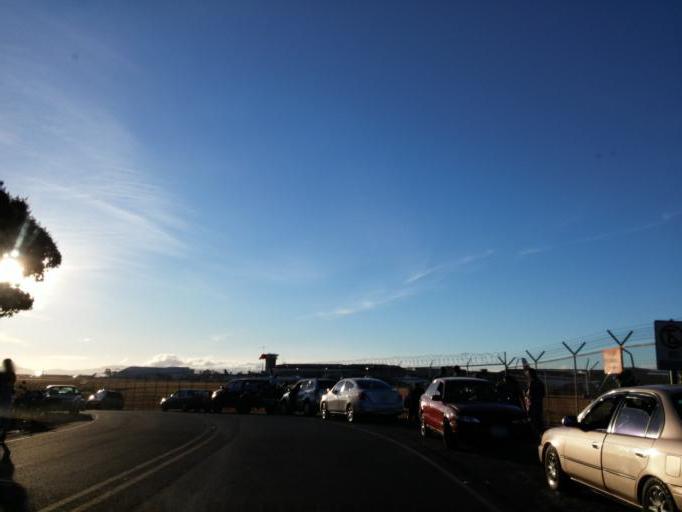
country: CR
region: Heredia
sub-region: Canton de Belen
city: San Antonio
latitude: 9.9963
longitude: -84.1991
